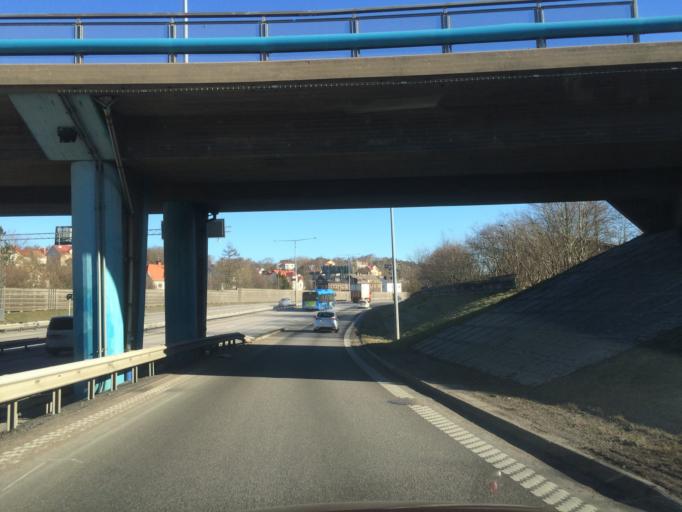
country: SE
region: Vaestra Goetaland
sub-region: Goteborg
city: Majorna
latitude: 57.6774
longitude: 11.8966
